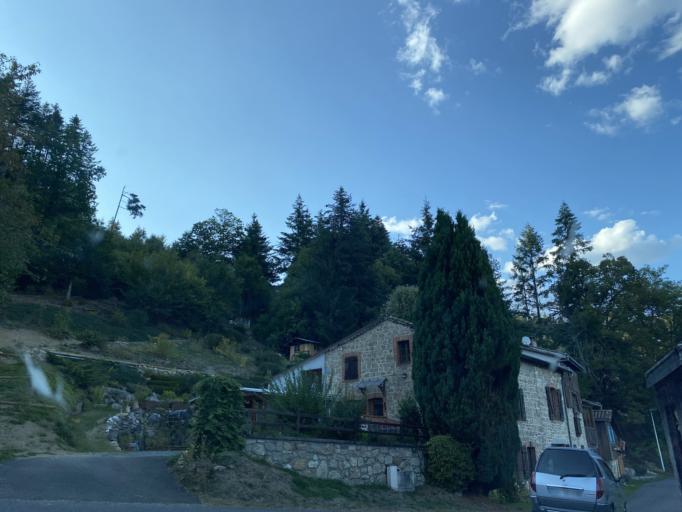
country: FR
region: Rhone-Alpes
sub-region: Departement de la Loire
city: Noiretable
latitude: 45.8104
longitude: 3.7533
